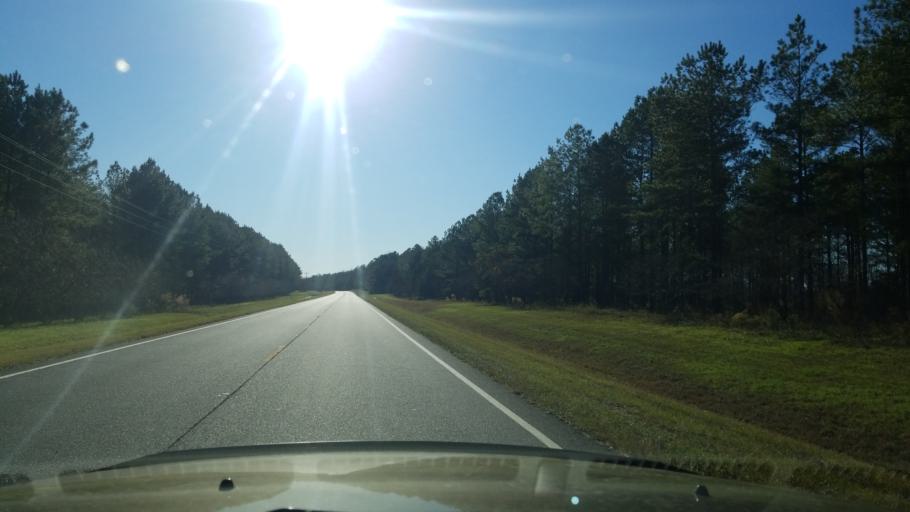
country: US
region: Georgia
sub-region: Talbot County
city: Talbotton
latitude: 32.6227
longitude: -84.5418
